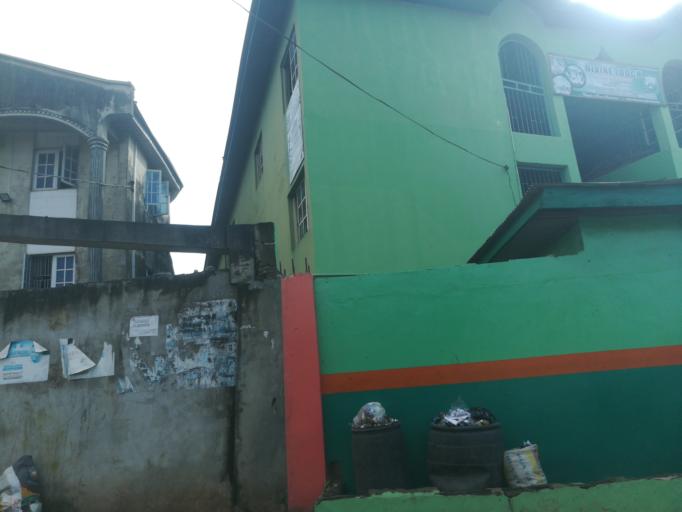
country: NG
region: Lagos
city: Agege
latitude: 6.6143
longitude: 3.3213
